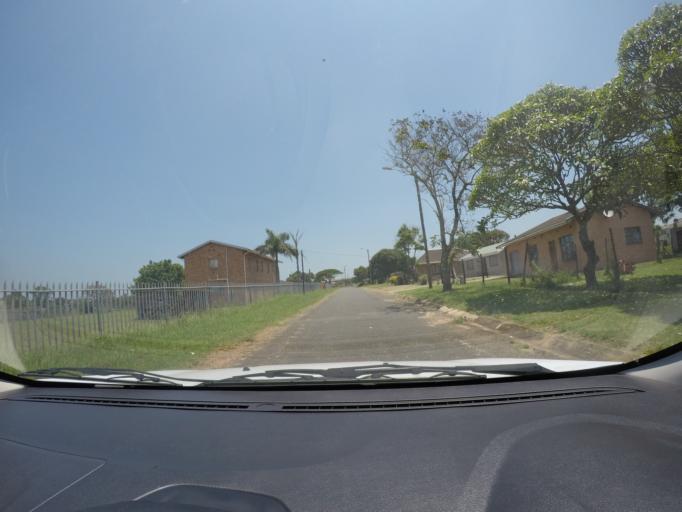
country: ZA
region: KwaZulu-Natal
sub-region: uThungulu District Municipality
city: eSikhawini
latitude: -28.8812
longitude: 31.8945
